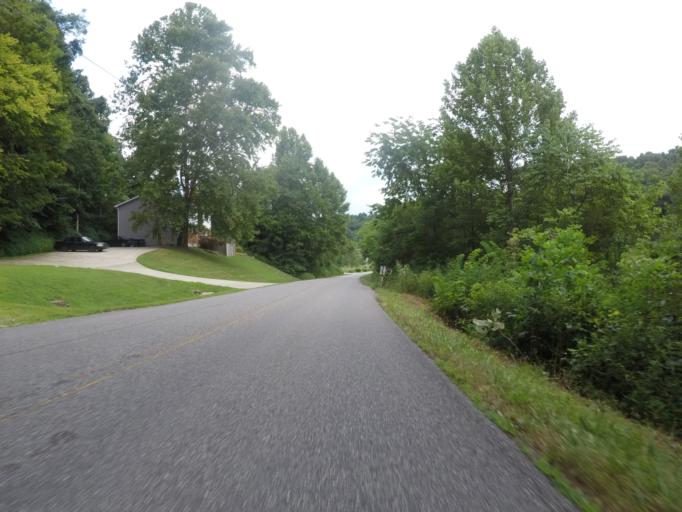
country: US
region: Kentucky
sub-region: Boyd County
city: Meads
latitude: 38.4231
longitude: -82.7082
